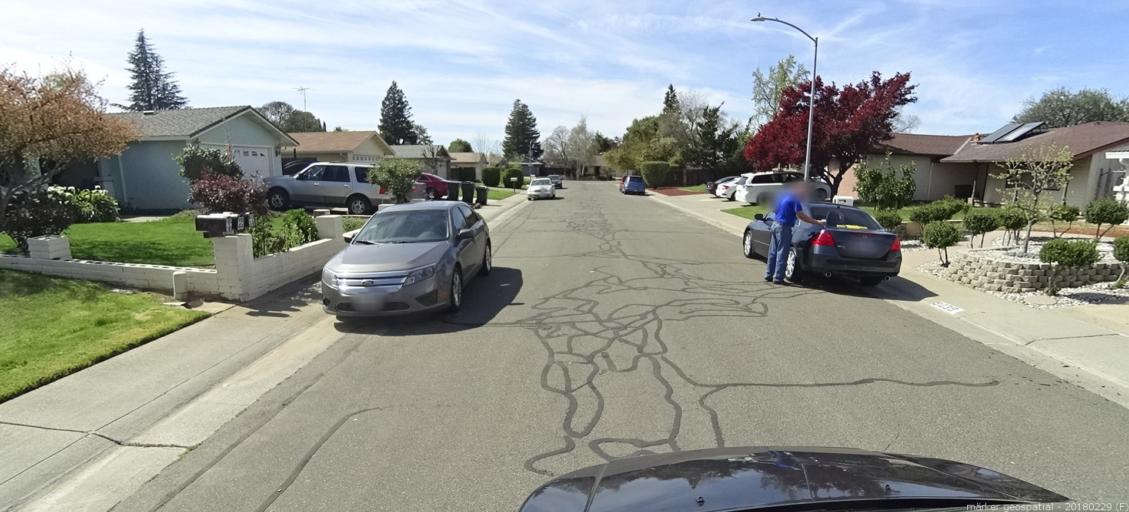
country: US
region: California
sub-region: Sacramento County
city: Rosemont
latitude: 38.5423
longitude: -121.3638
